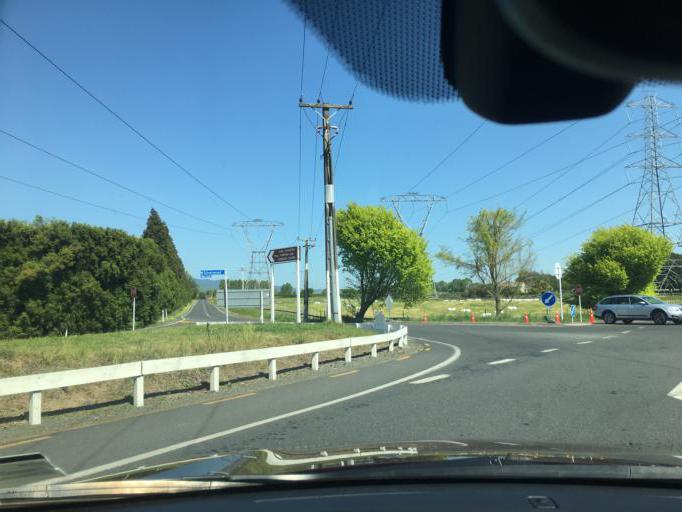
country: NZ
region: Waikato
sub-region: Waipa District
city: Cambridge
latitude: -37.9065
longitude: 175.4511
